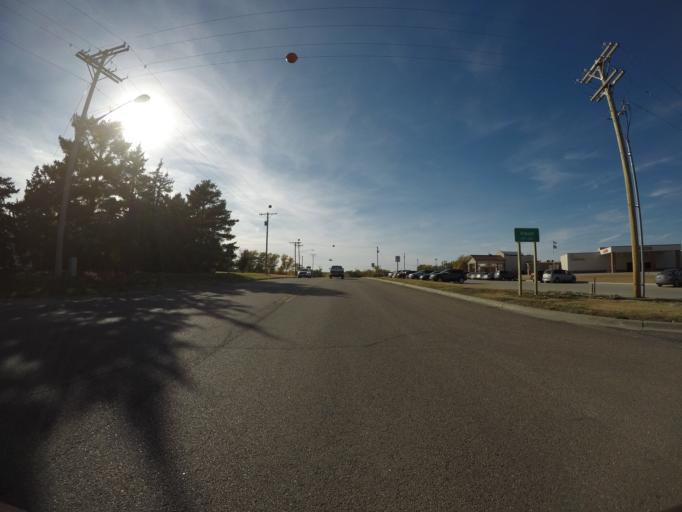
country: US
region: Kansas
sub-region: Rawlins County
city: Atwood
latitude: 39.8133
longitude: -101.0374
